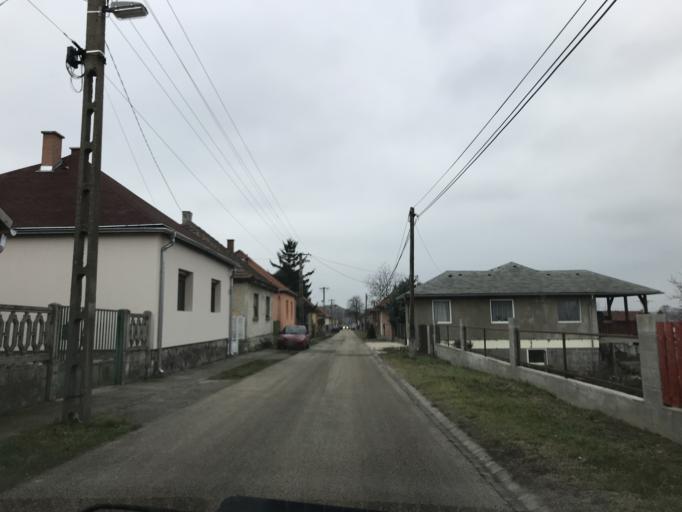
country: HU
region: Komarom-Esztergom
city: Tokod
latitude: 47.7276
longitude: 18.6650
